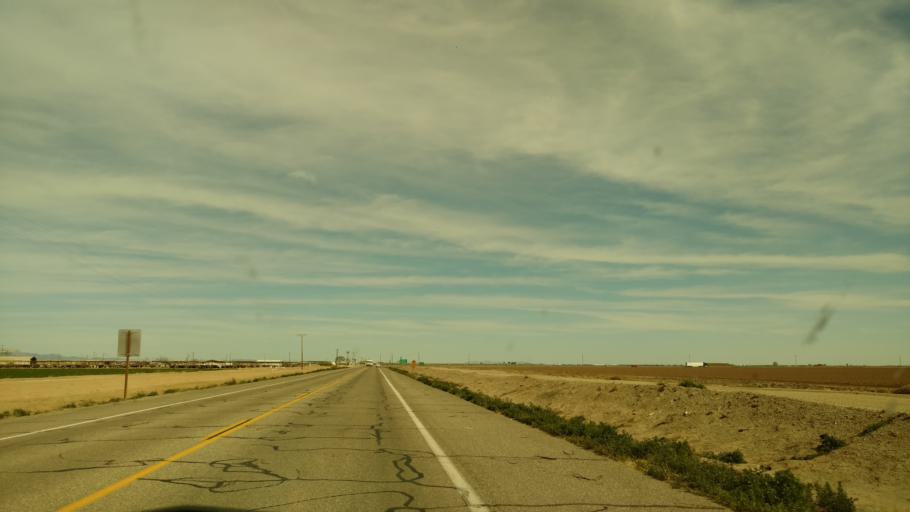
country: US
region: California
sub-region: Imperial County
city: Brawley
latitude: 32.9745
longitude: -115.4133
